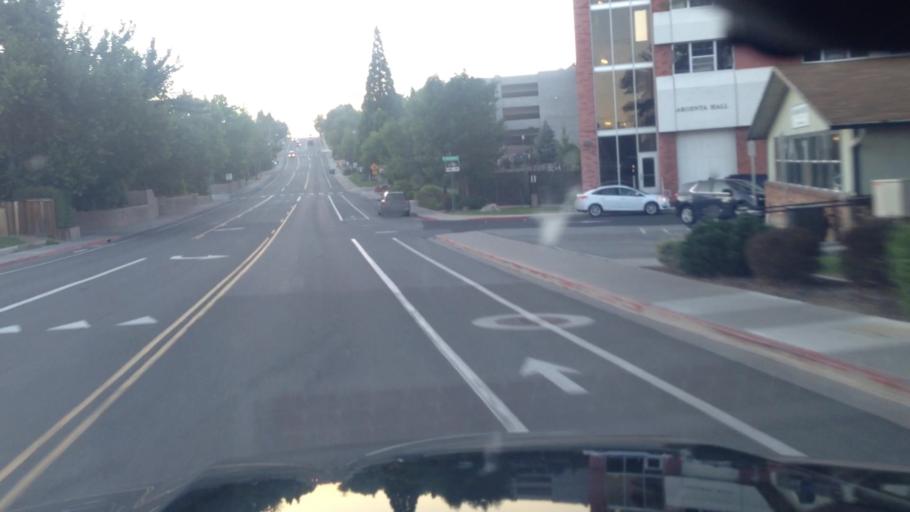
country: US
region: Nevada
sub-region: Washoe County
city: Reno
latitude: 39.5383
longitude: -119.8186
